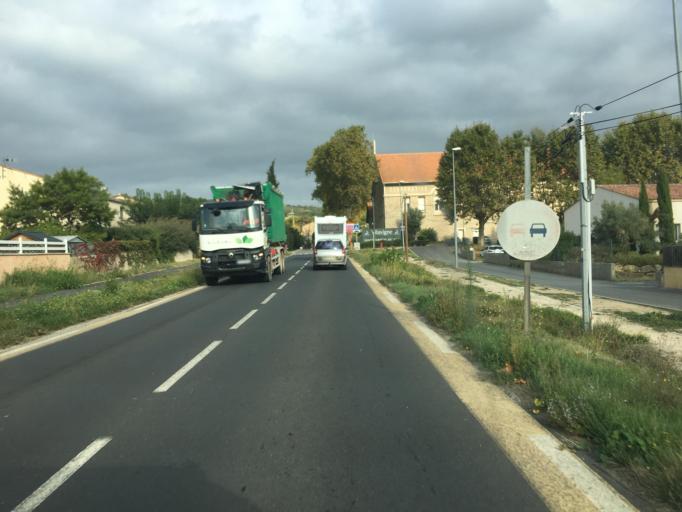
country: FR
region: Languedoc-Roussillon
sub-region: Departement de l'Herault
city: Nebian
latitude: 43.6031
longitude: 3.4384
